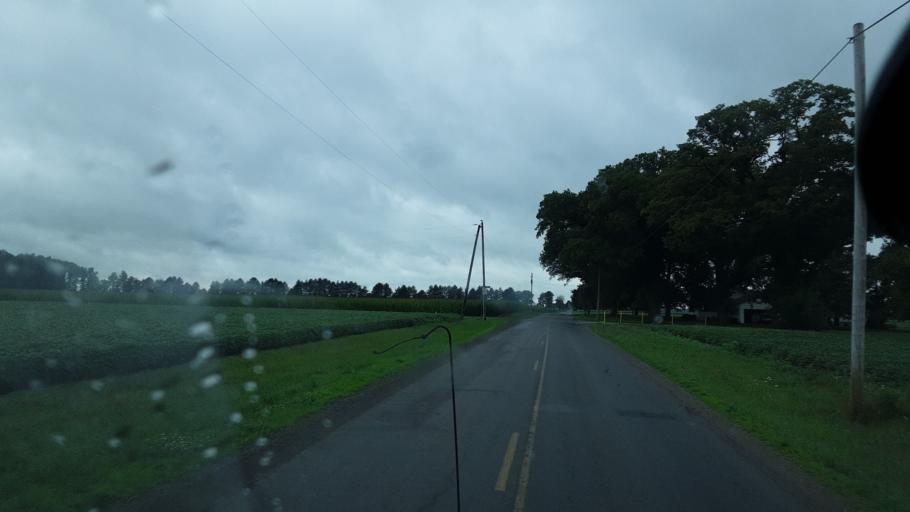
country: US
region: Ohio
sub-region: Van Wert County
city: Van Wert
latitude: 40.8003
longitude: -84.6279
